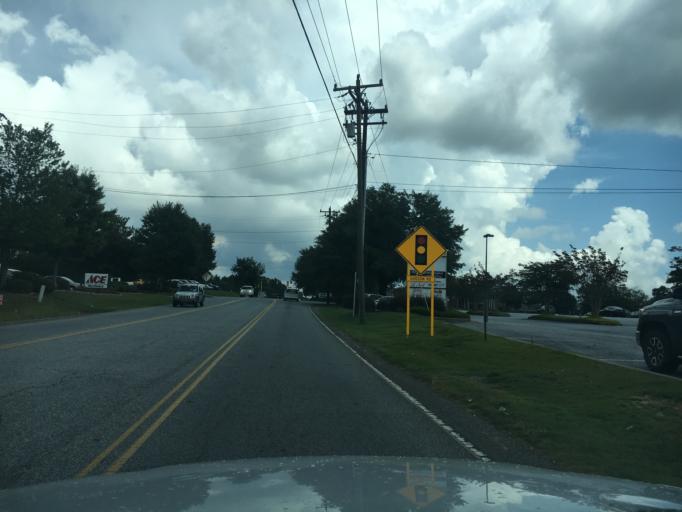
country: US
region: South Carolina
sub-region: Greenville County
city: Taylors
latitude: 34.8925
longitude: -82.2922
